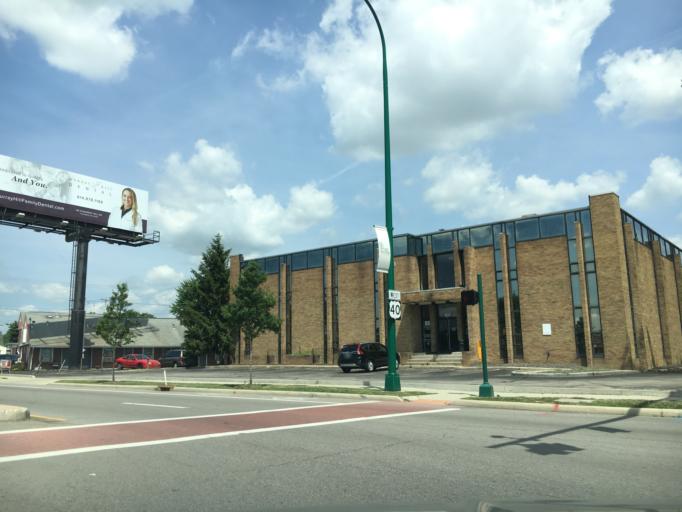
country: US
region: Ohio
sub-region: Franklin County
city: Lincoln Village
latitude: 39.9517
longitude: -83.1396
